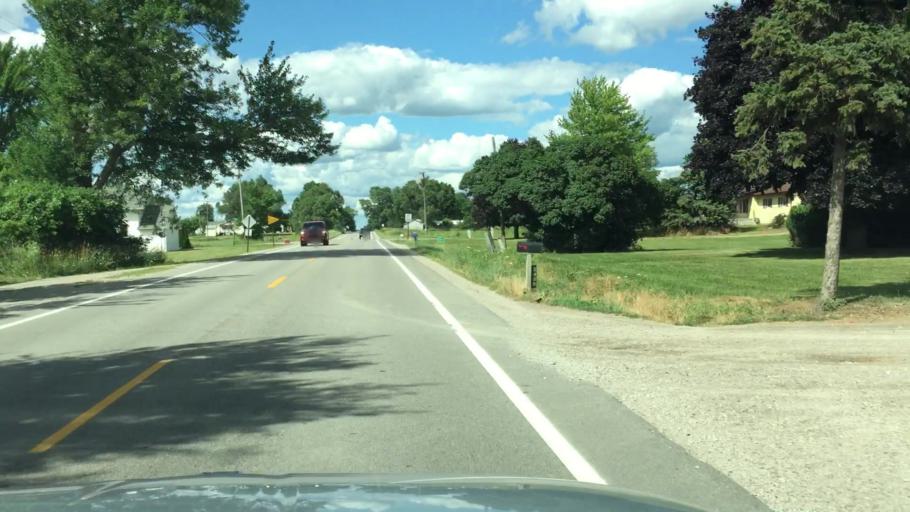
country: US
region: Michigan
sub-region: Saint Clair County
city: Capac
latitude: 42.9667
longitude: -82.9365
